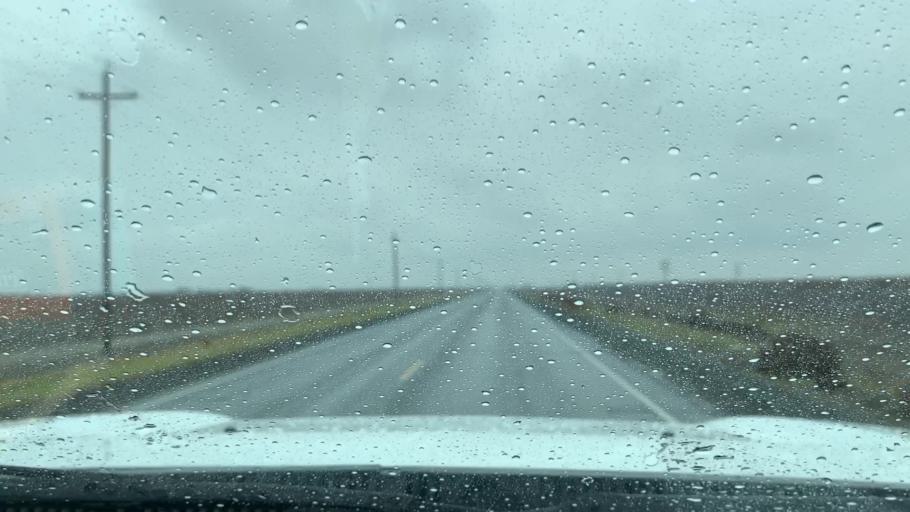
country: US
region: California
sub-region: Kings County
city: Corcoran
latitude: 36.0169
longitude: -119.4969
